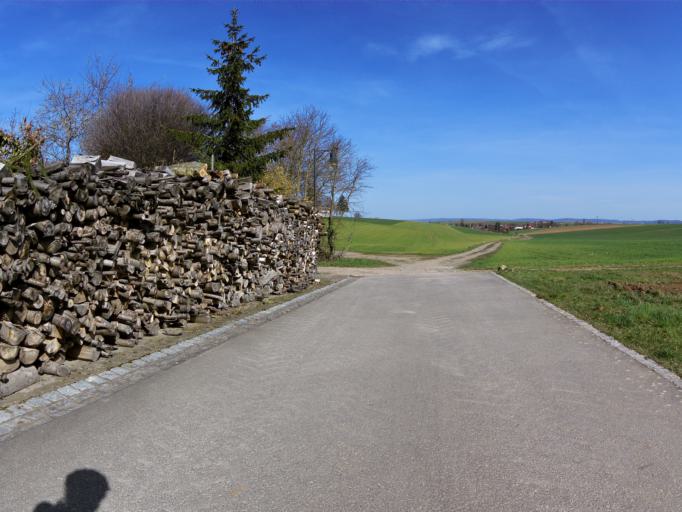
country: DE
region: Bavaria
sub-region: Regierungsbezirk Unterfranken
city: Biebelried
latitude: 49.7961
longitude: 10.0900
